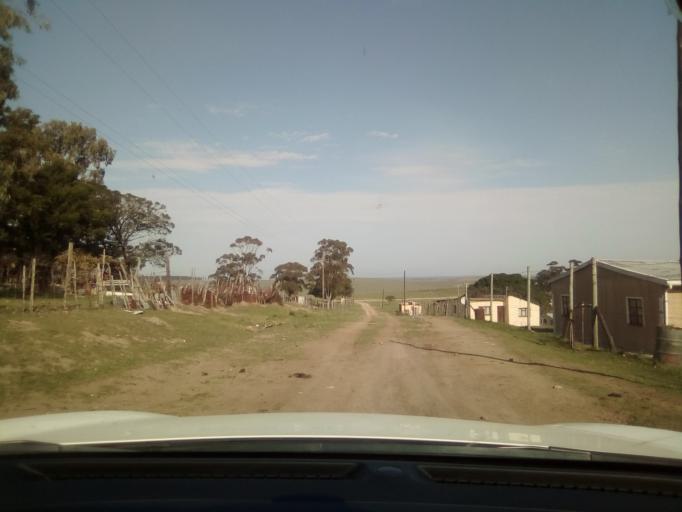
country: ZA
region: Eastern Cape
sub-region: Buffalo City Metropolitan Municipality
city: Bhisho
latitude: -32.9849
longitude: 27.2582
